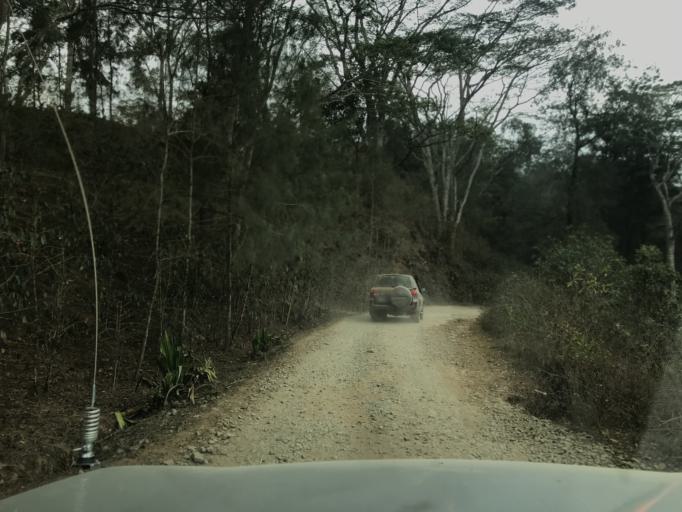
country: TL
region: Ermera
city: Gleno
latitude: -8.8205
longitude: 125.4336
